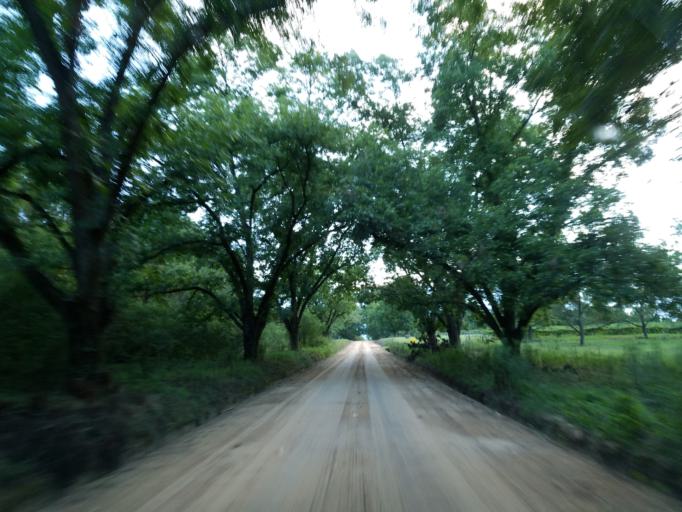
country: US
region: Georgia
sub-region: Tift County
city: Tifton
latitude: 31.5308
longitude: -83.5073
